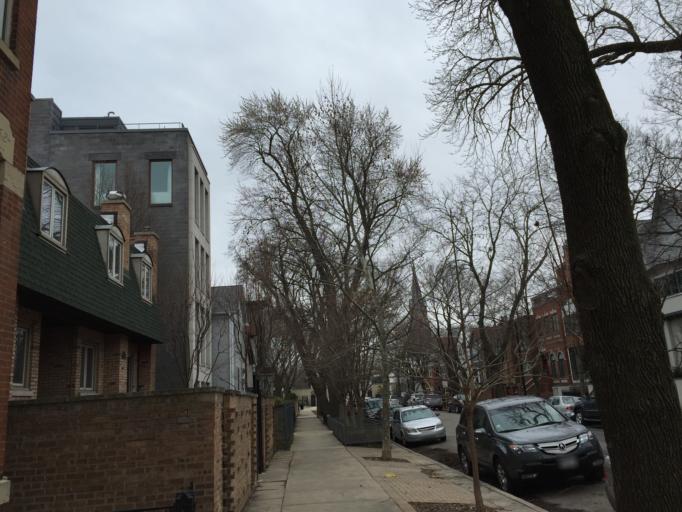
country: US
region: Illinois
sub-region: Cook County
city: Chicago
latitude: 41.9158
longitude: -87.6398
